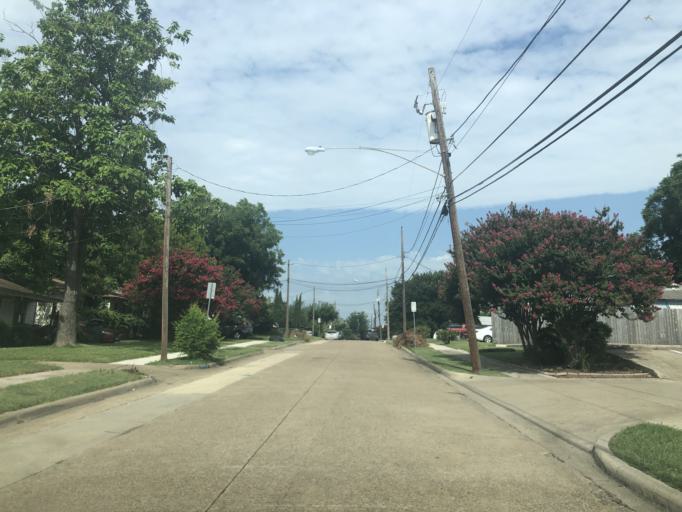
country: US
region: Texas
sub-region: Dallas County
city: Dallas
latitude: 32.8158
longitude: -96.8485
